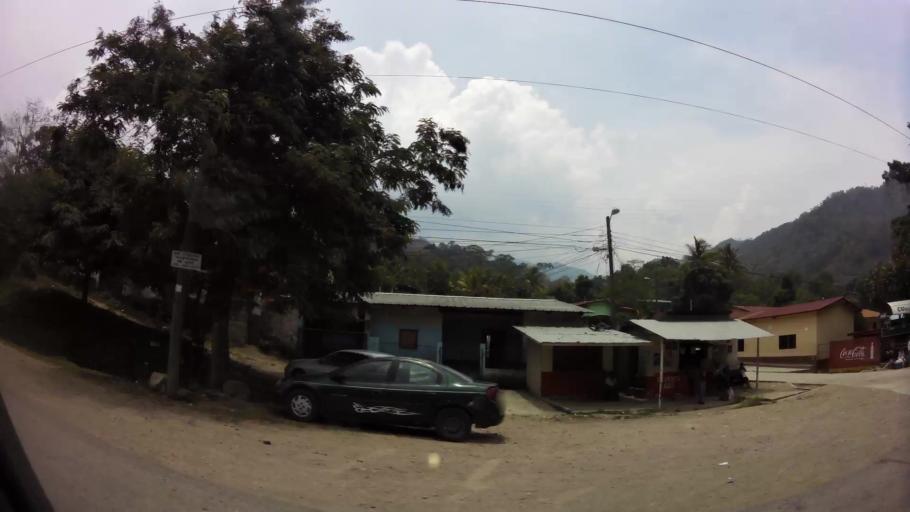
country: HN
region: Comayagua
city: Taulabe
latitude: 14.7481
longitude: -87.9594
